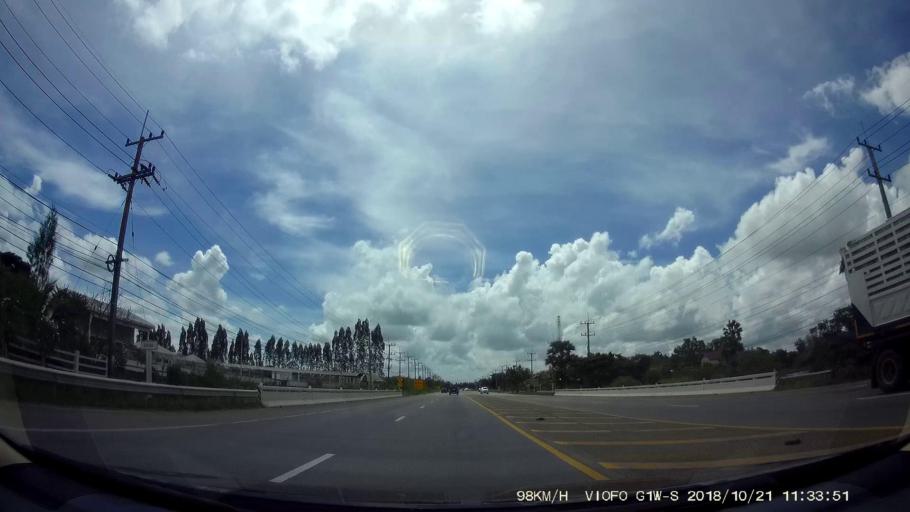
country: TH
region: Chaiyaphum
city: Chaiyaphum
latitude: 15.7398
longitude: 102.0243
